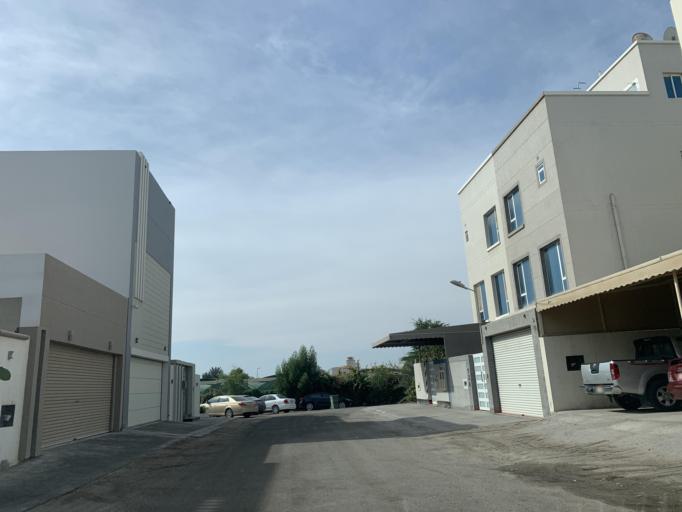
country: BH
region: Central Governorate
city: Madinat Hamad
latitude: 26.1285
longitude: 50.4719
